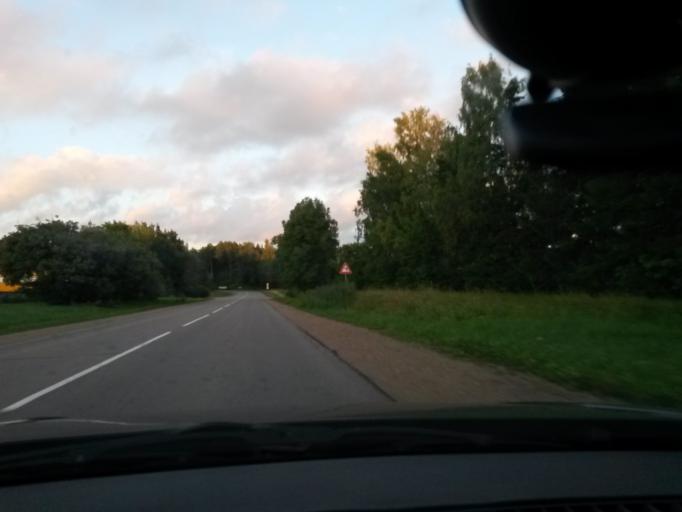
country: LV
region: Madonas Rajons
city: Madona
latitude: 56.8052
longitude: 26.0780
